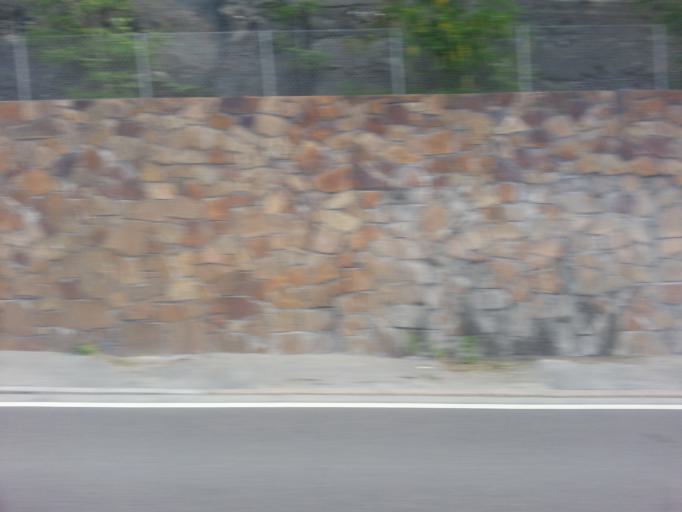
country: NO
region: Oslo
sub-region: Oslo
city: Sjolyststranda
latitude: 59.9188
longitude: 10.6672
